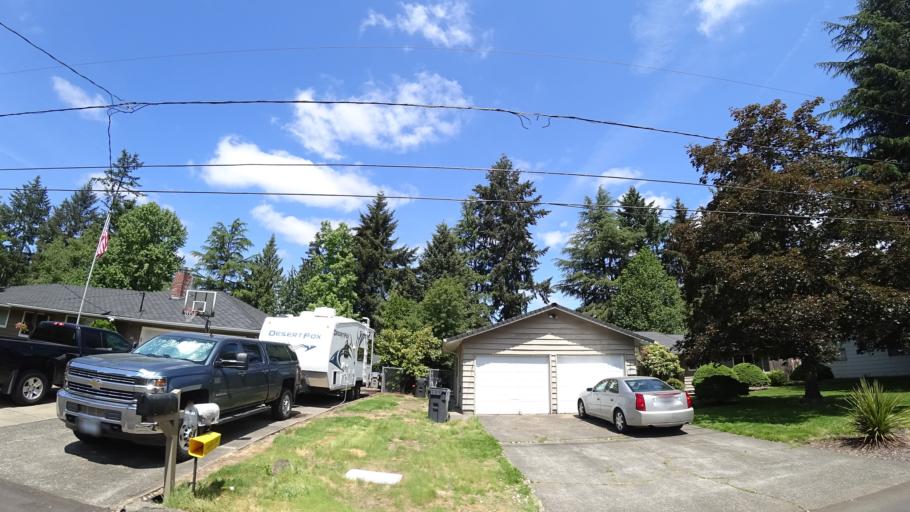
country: US
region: Oregon
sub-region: Washington County
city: King City
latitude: 45.4264
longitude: -122.8015
